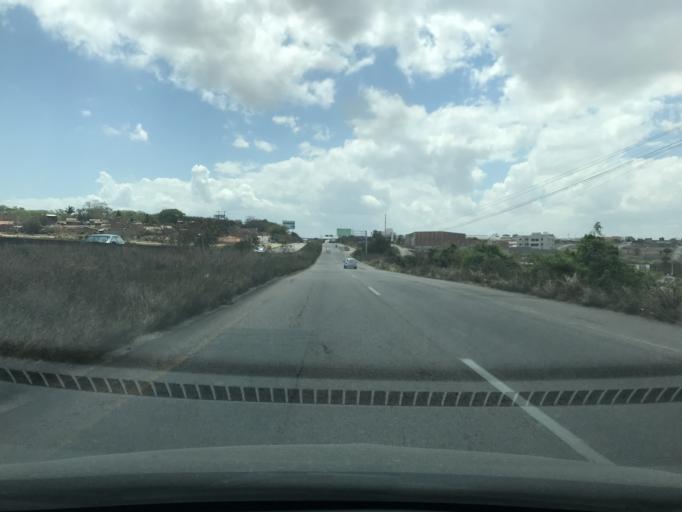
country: BR
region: Pernambuco
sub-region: Caruaru
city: Caruaru
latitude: -8.3084
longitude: -35.9541
